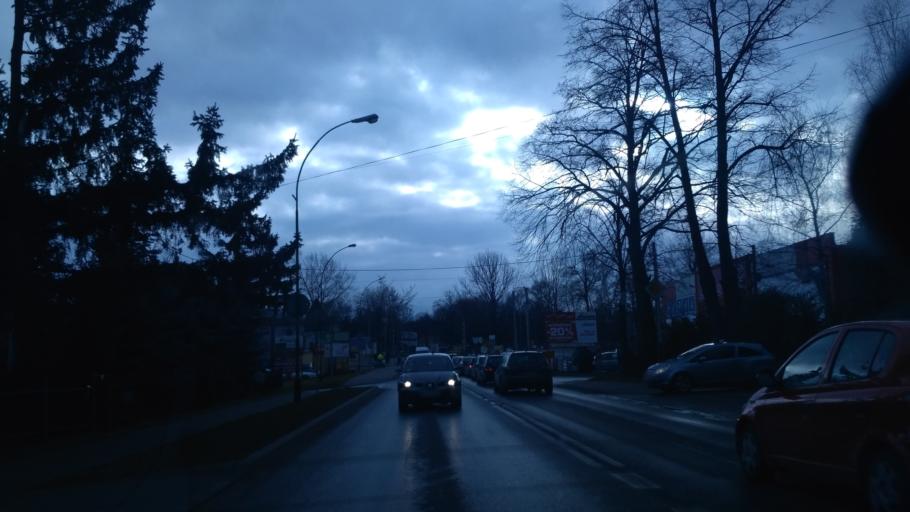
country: PL
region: Subcarpathian Voivodeship
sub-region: Powiat lancucki
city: Lancut
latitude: 50.0832
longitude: 22.2327
